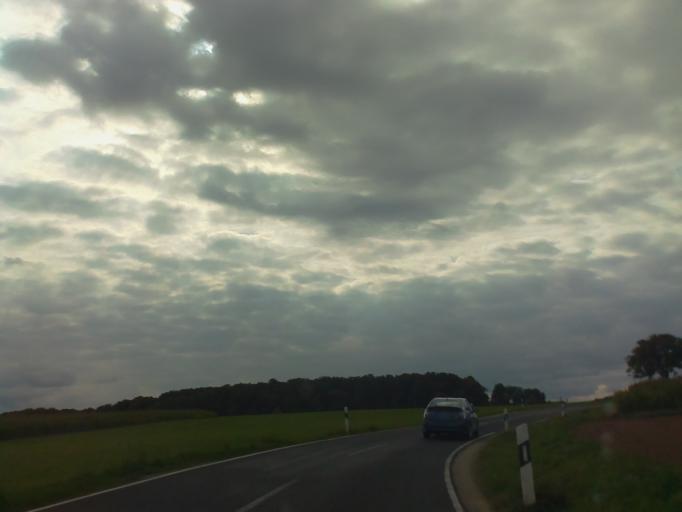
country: DE
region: Hesse
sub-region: Regierungsbezirk Kassel
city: Eiterfeld
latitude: 50.7484
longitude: 9.7518
